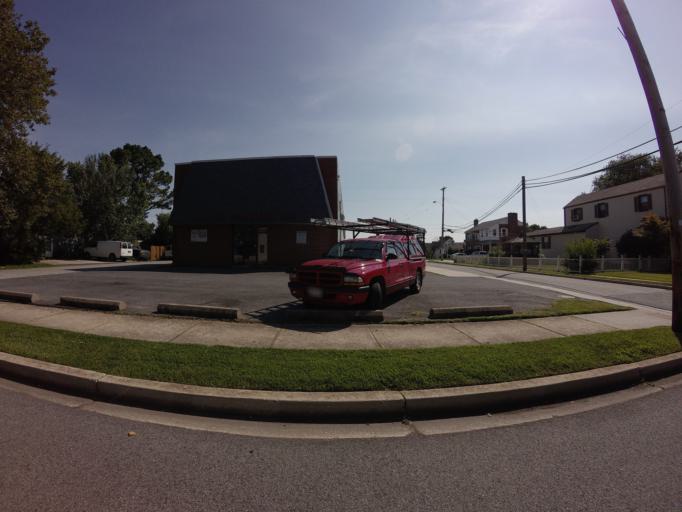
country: US
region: Maryland
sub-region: Baltimore County
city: Edgemere
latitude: 39.2420
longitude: -76.4489
